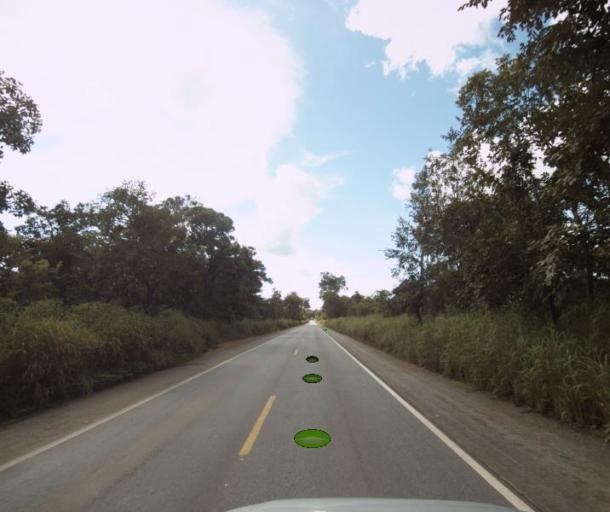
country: BR
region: Goias
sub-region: Porangatu
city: Porangatu
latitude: -13.1219
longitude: -49.1986
